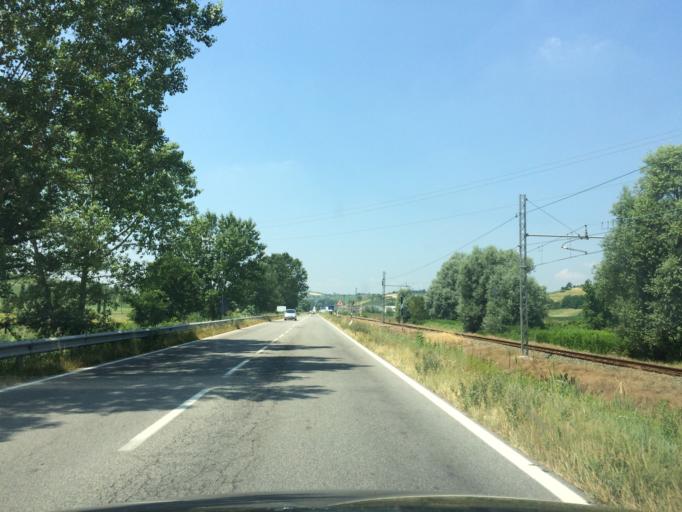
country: IT
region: Piedmont
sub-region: Provincia di Asti
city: Castelnuovo Calcea
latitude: 44.7762
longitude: 8.2910
